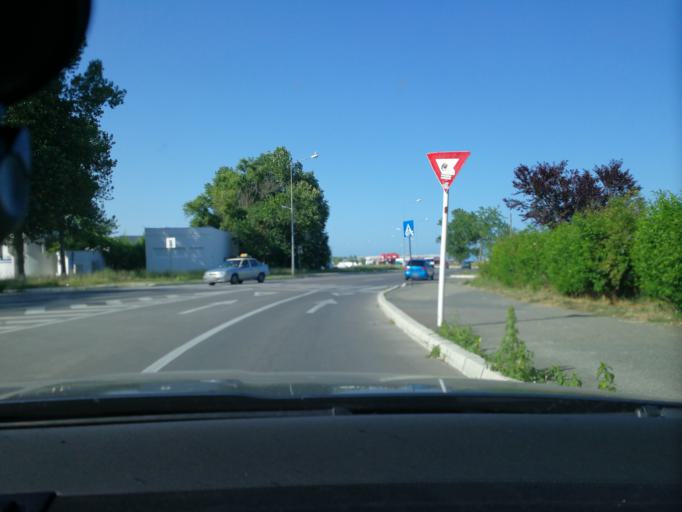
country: RO
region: Constanta
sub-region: Municipiul Mangalia
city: Mangalia
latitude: 43.8309
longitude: 28.5867
